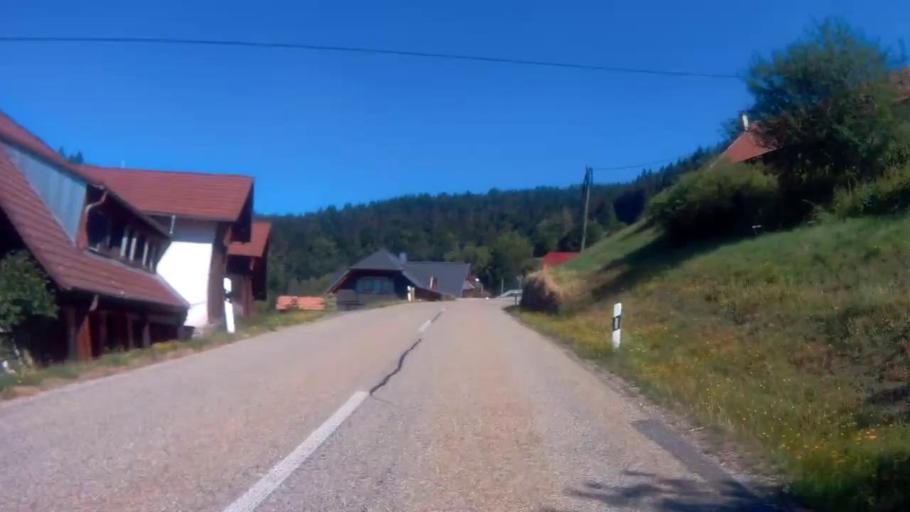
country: DE
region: Baden-Wuerttemberg
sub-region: Freiburg Region
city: Sulzburg
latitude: 47.7649
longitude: 7.7532
